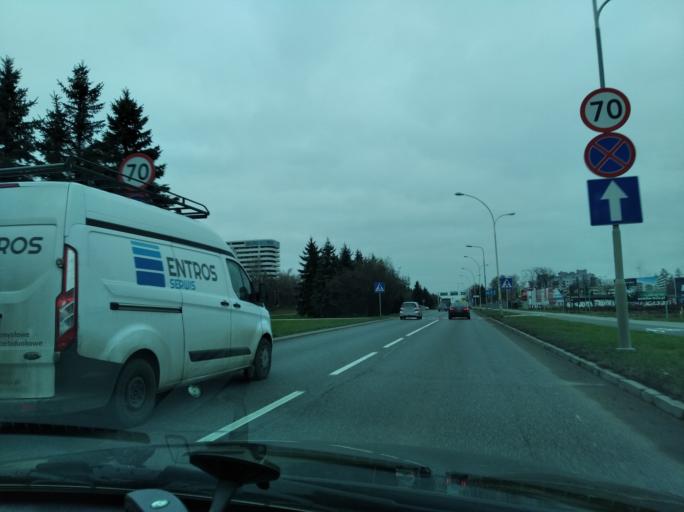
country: PL
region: Subcarpathian Voivodeship
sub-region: Rzeszow
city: Rzeszow
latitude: 50.0421
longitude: 21.9794
